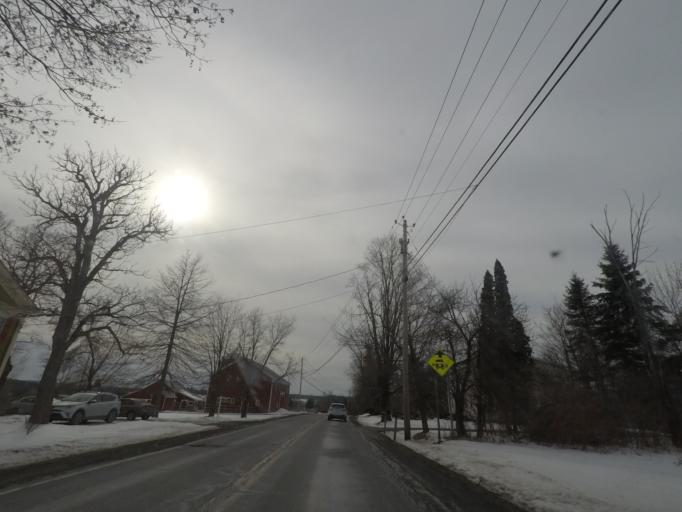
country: US
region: New York
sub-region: Albany County
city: Altamont
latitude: 42.6664
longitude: -74.1246
